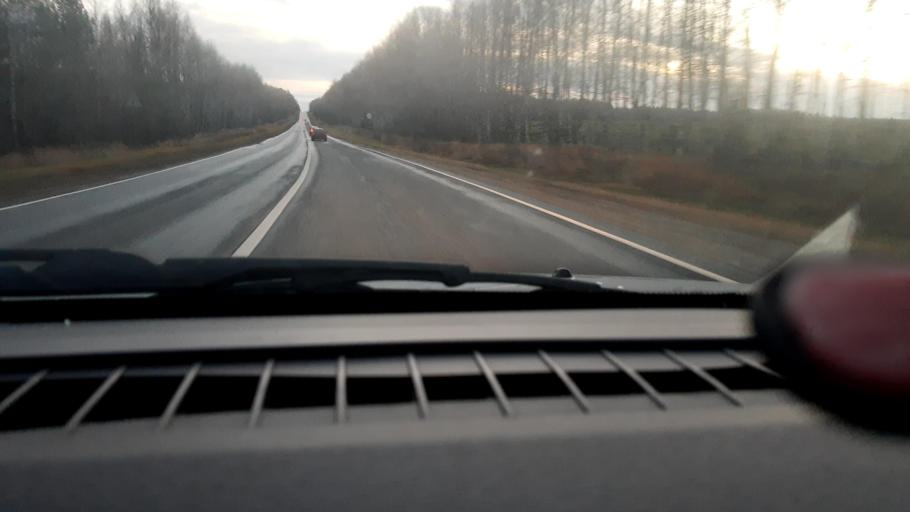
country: RU
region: Nizjnij Novgorod
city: Vladimirskoye
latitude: 56.9562
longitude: 45.0945
